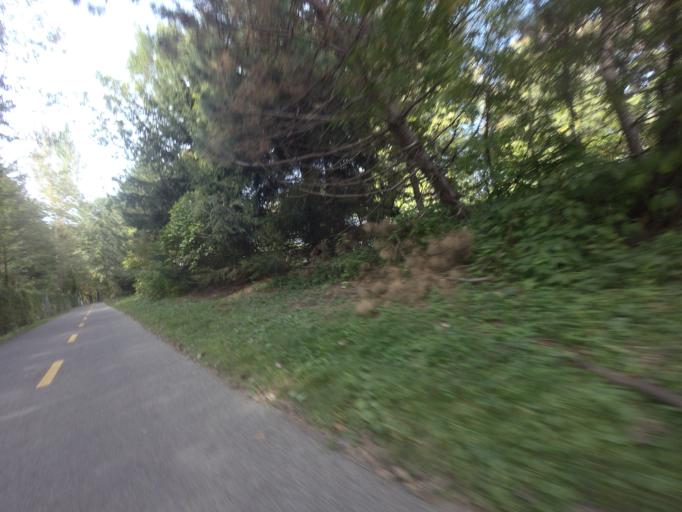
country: CA
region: Quebec
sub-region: Laurentides
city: Blainville
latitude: 45.7023
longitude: -73.9058
